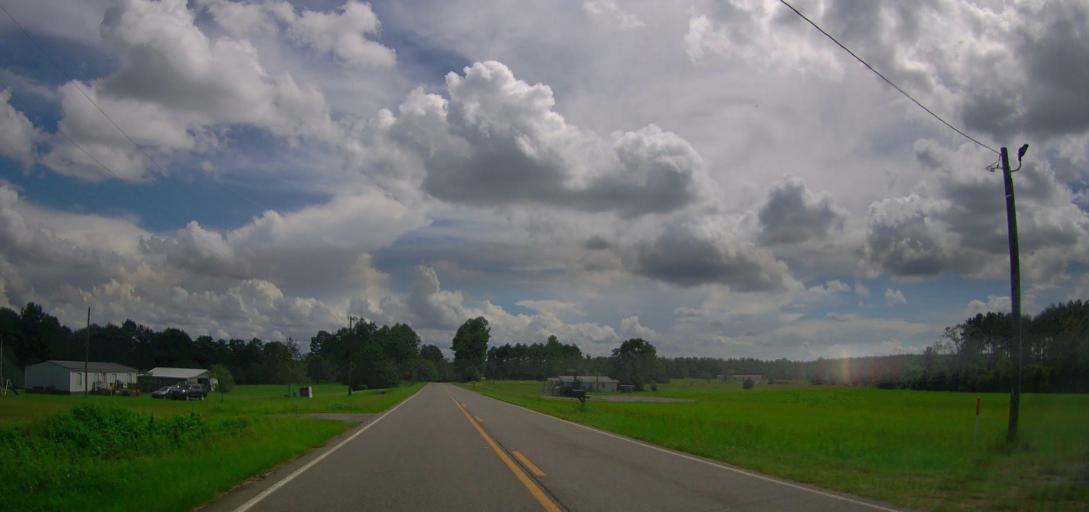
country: US
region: Georgia
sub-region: Taylor County
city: Butler
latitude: 32.4676
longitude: -84.1998
